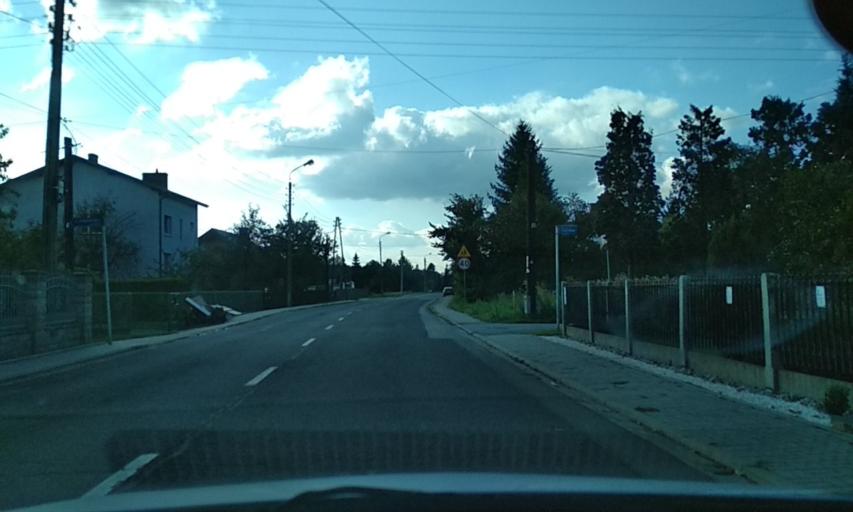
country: PL
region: Silesian Voivodeship
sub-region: Powiat bierunsko-ledzinski
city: Ledziny
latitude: 50.1707
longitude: 19.1523
